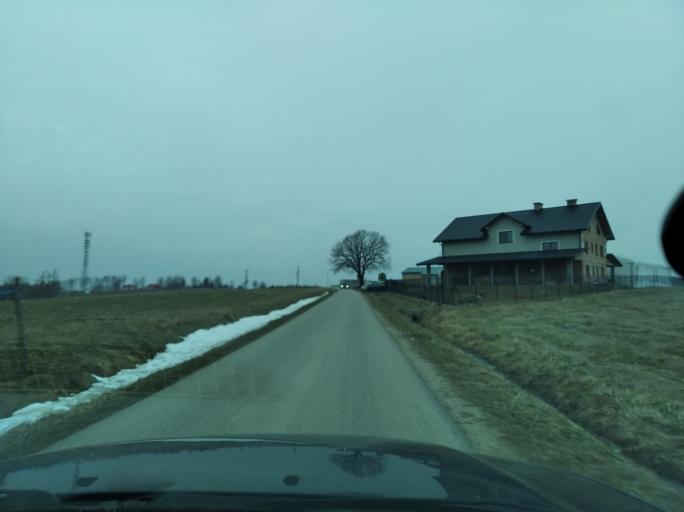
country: PL
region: Subcarpathian Voivodeship
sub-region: Powiat rzeszowski
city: Chmielnik
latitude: 49.9855
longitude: 22.1528
